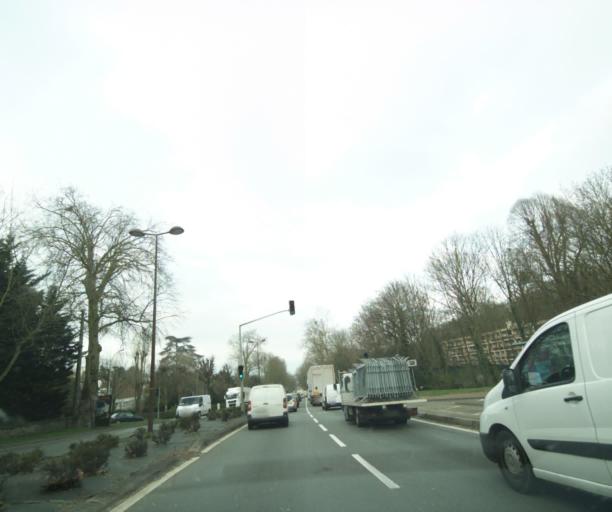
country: FR
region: Ile-de-France
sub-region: Departement des Yvelines
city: Le Port-Marly
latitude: 48.8749
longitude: 2.1026
